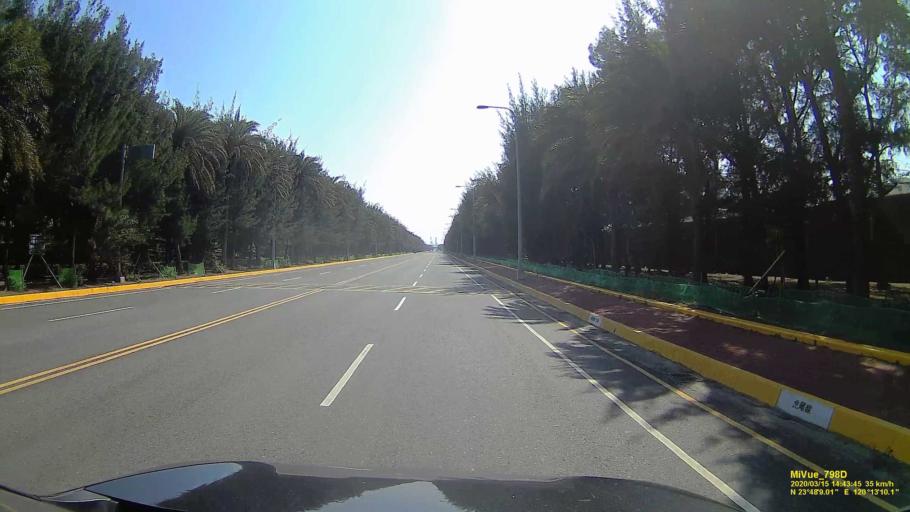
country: TW
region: Taiwan
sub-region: Yunlin
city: Douliu
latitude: 23.8024
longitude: 120.2194
